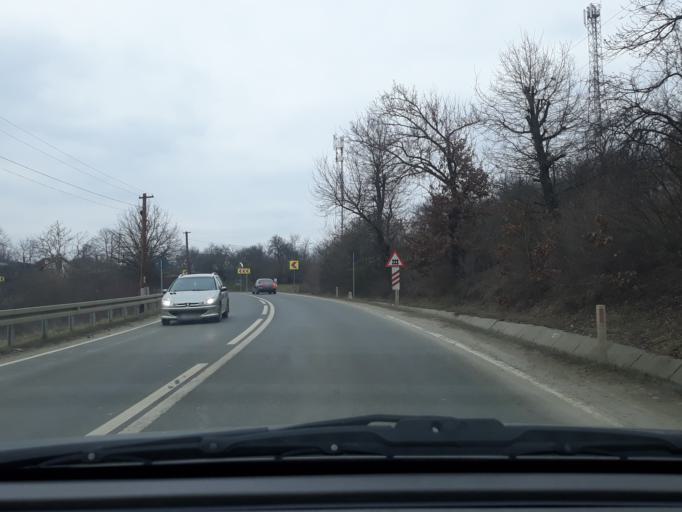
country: RO
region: Salaj
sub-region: Comuna Nusfalau
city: Nusfalau
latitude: 47.2075
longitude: 22.7190
